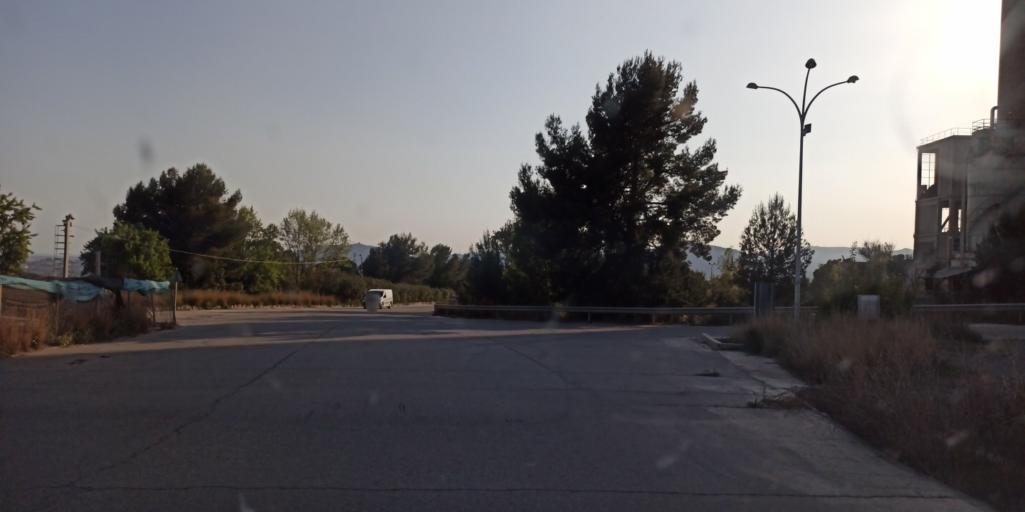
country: ES
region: Catalonia
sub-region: Provincia de Barcelona
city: Sant Feliu de Llobregat
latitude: 41.4003
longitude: 2.0558
